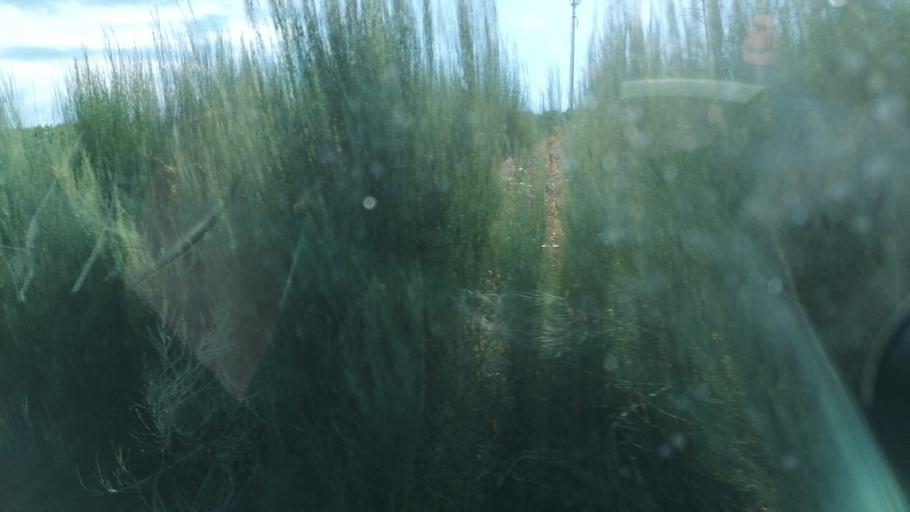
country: PT
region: Vila Real
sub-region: Sabrosa
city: Sabrosa
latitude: 41.3573
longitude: -7.5901
